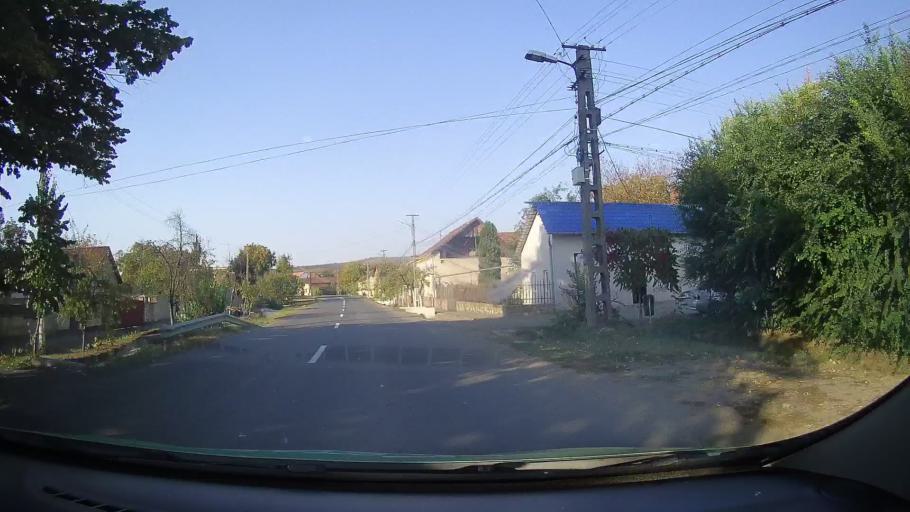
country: RO
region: Arad
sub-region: Comuna Ghioroc
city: Ghioroc
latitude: 46.1367
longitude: 21.6047
